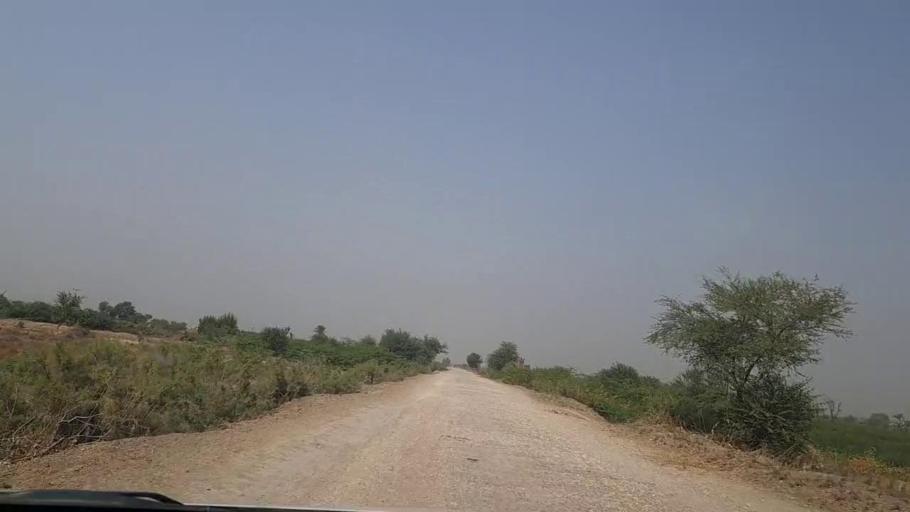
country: PK
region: Sindh
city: Mirpur Khas
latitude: 25.5940
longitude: 69.2010
